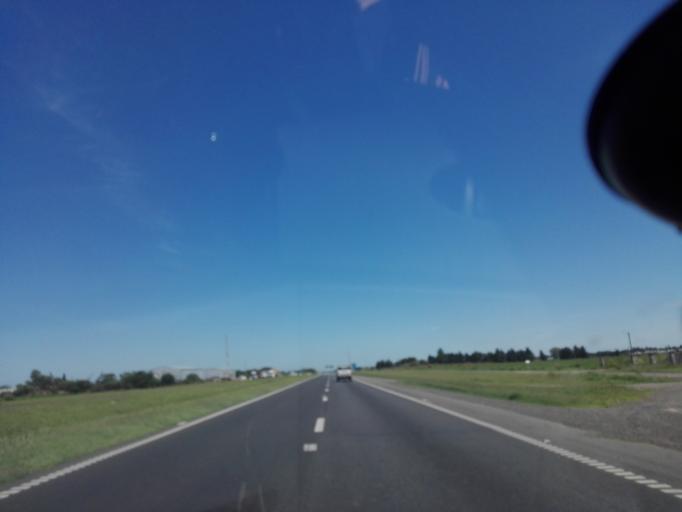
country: AR
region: Buenos Aires
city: San Nicolas de los Arroyos
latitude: -33.3728
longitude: -60.2435
